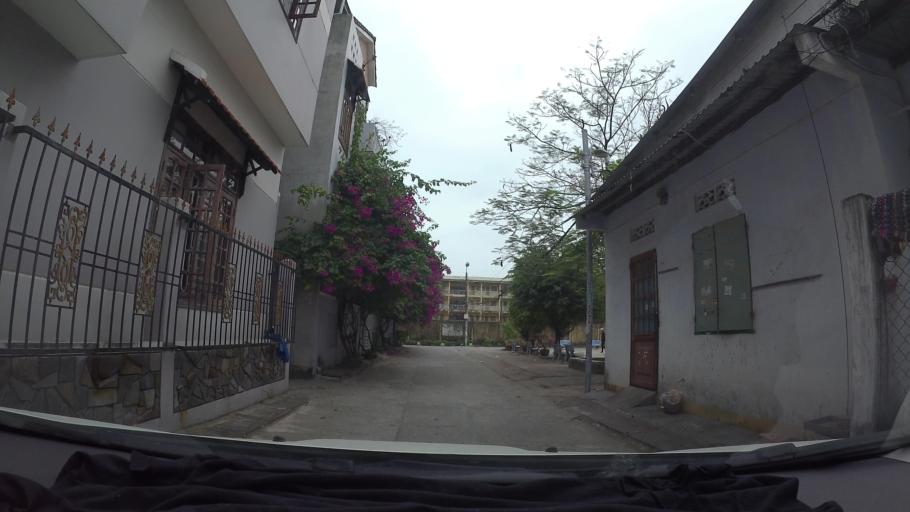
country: VN
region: Da Nang
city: Lien Chieu
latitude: 16.0727
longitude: 108.1523
